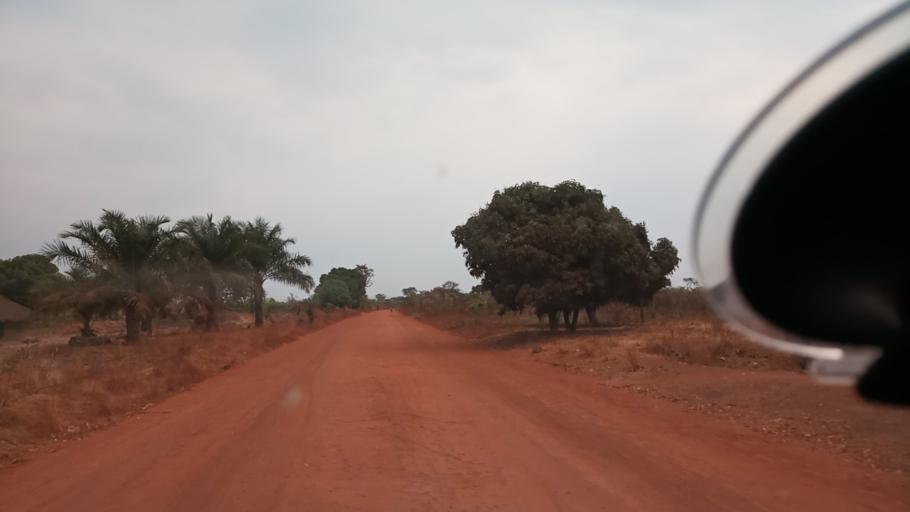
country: ZM
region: Luapula
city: Nchelenge
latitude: -9.1482
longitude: 28.2902
